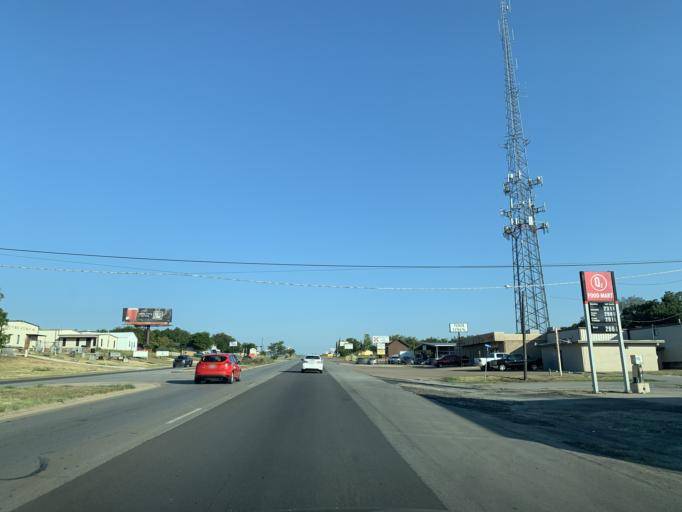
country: US
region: Texas
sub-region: Tarrant County
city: Sansom Park
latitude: 32.8009
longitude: -97.4077
